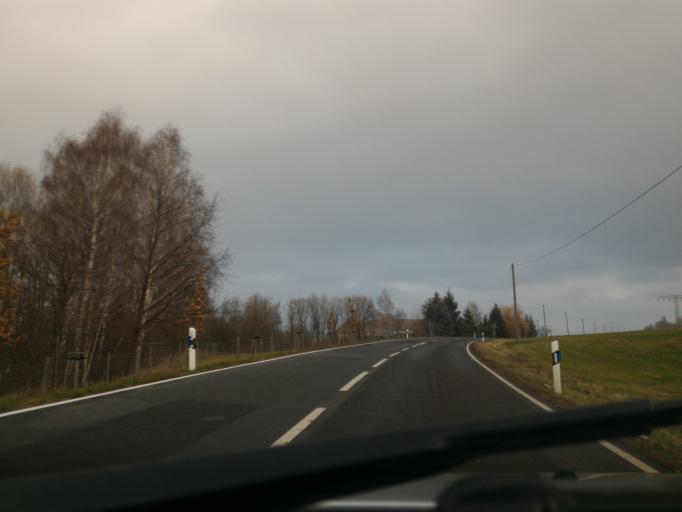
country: DE
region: Saxony
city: Grossschonau
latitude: 50.8948
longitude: 14.6927
